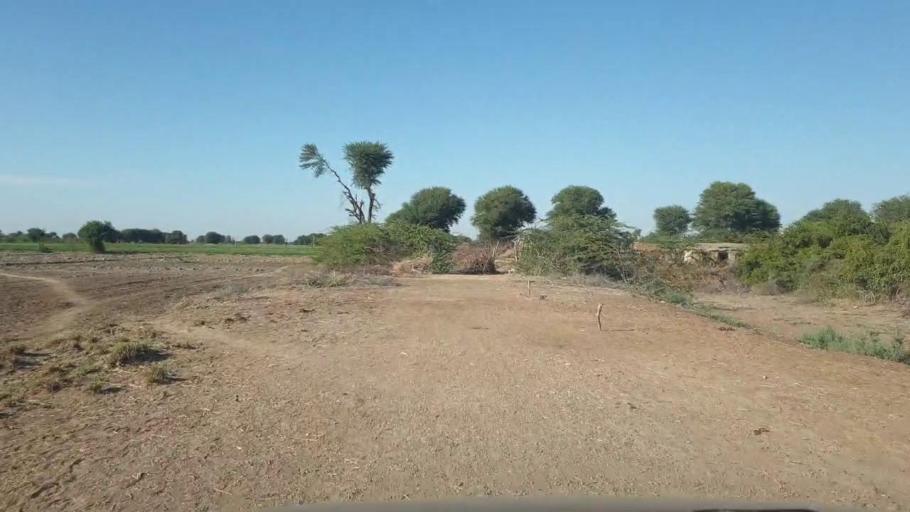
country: PK
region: Sindh
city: Dhoro Naro
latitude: 25.4336
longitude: 69.5438
